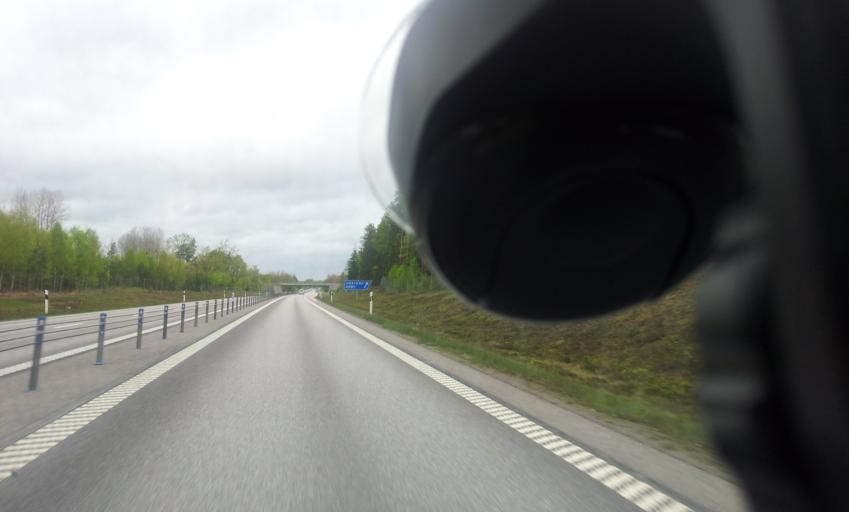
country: SE
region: Kalmar
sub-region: Kalmar Kommun
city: Ljungbyholm
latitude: 56.5463
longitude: 16.0842
